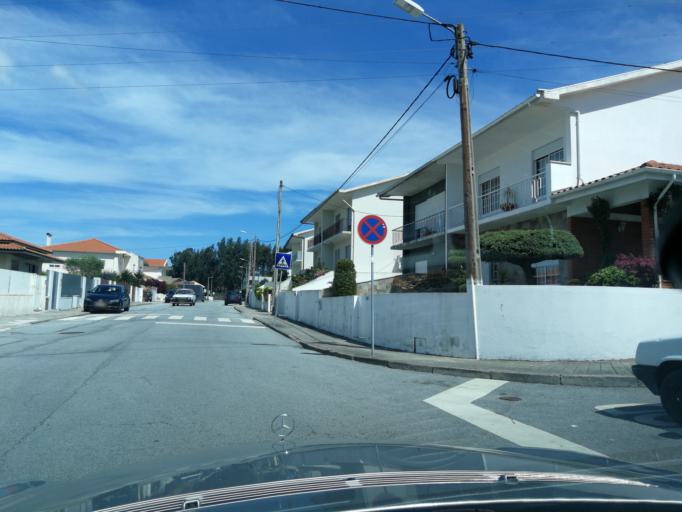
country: PT
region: Braga
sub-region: Vila Nova de Famalicao
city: Vila Nova de Famalicao
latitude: 41.4181
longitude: -8.5143
